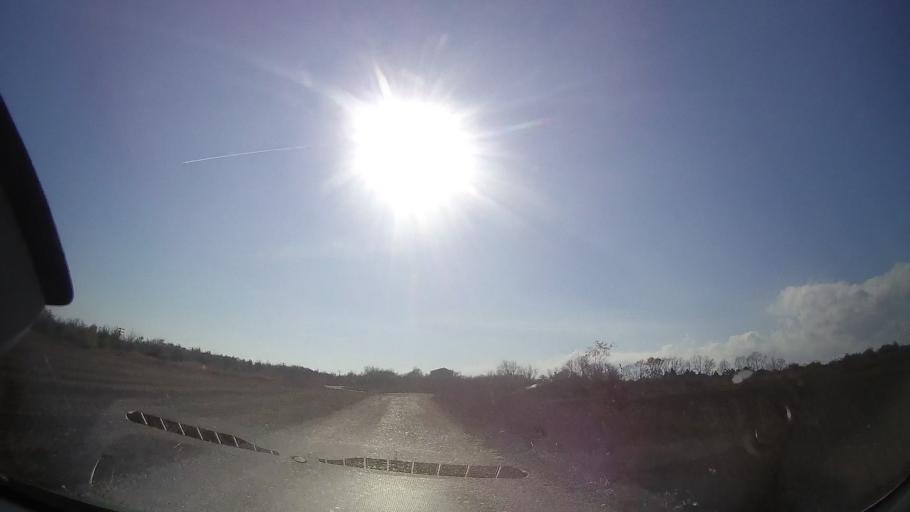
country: RO
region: Constanta
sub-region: Comuna Douazeci si Trei August
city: Douazeci si Trei August
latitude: 43.9052
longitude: 28.6186
